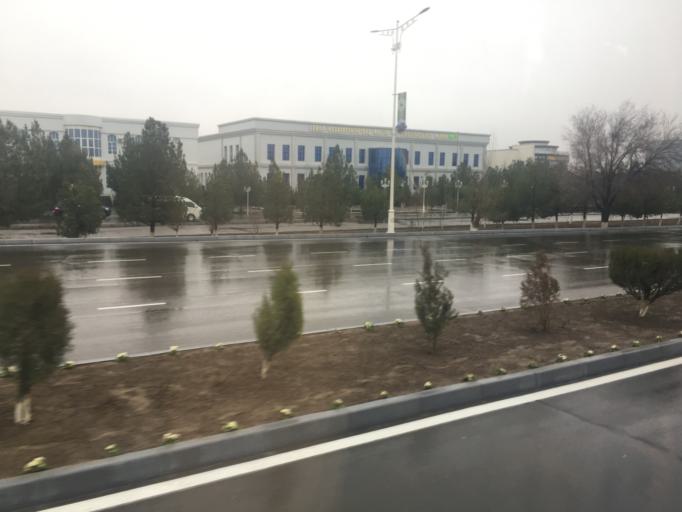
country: TM
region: Lebap
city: Turkmenabat
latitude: 39.0742
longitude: 63.5867
